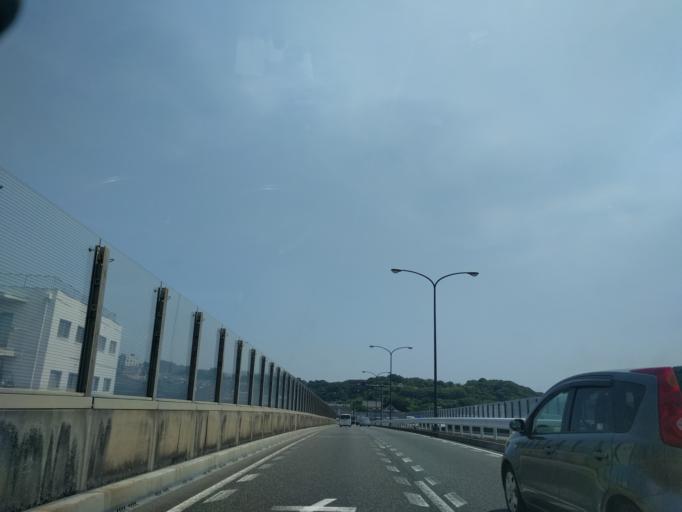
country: JP
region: Kanagawa
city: Yokohama
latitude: 35.3964
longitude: 139.5826
